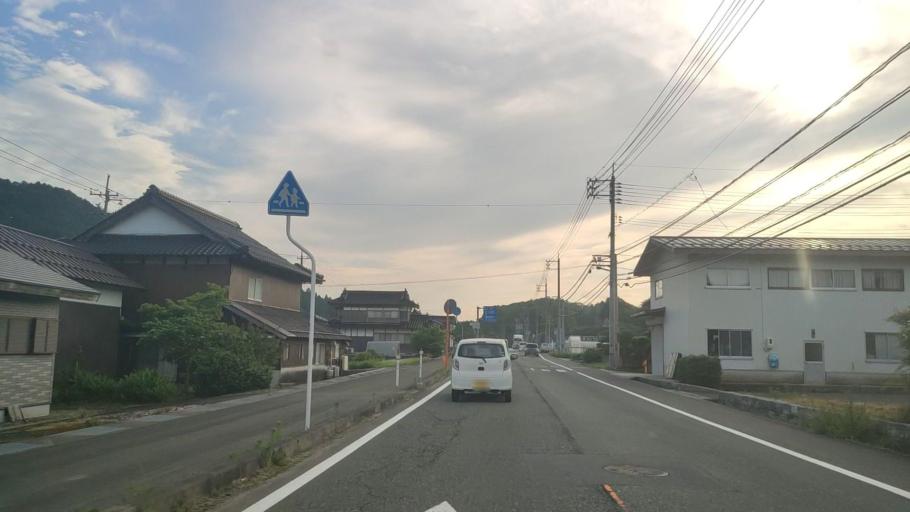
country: JP
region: Tottori
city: Kurayoshi
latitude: 35.2890
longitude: 133.7110
